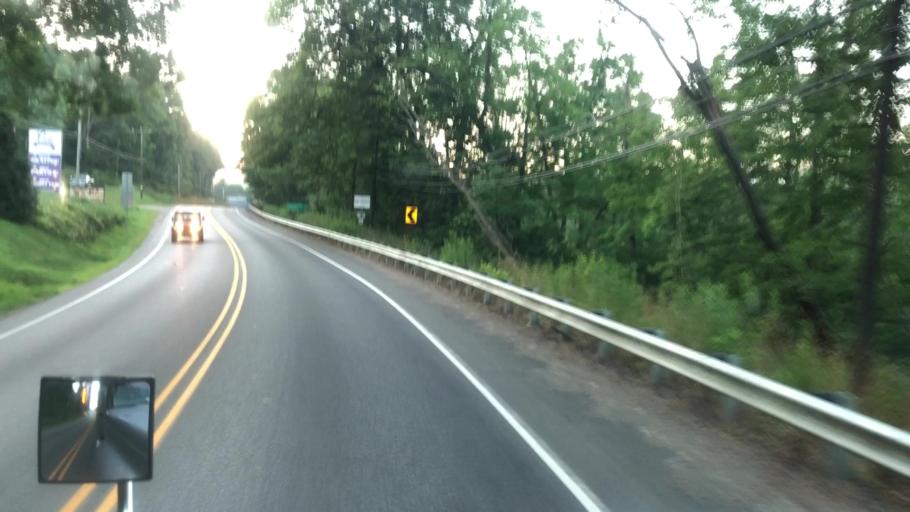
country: US
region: Pennsylvania
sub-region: Crawford County
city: Titusville
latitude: 41.6242
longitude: -79.6502
